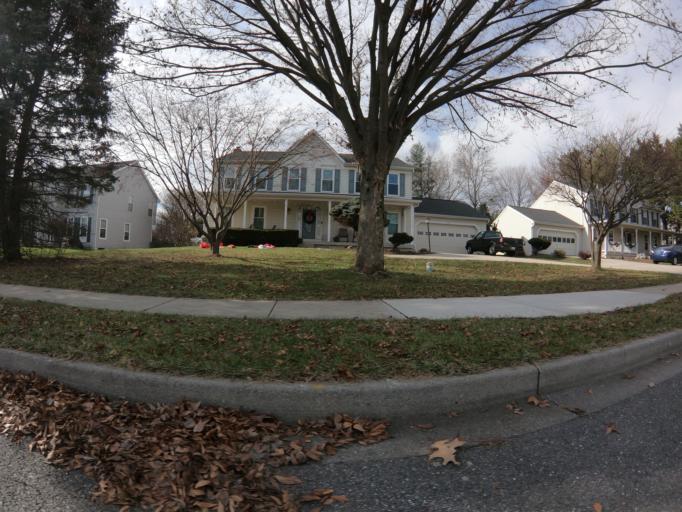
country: US
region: Maryland
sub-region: Frederick County
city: Ballenger Creek
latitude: 39.3806
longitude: -77.4296
